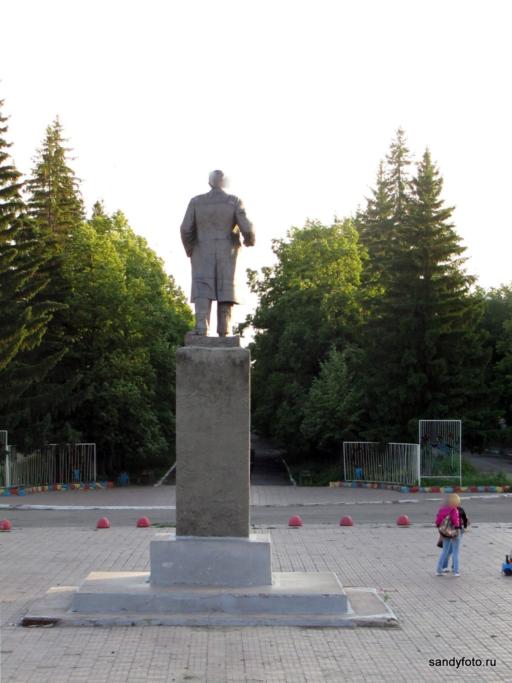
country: RU
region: Chelyabinsk
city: Troitsk
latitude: 54.0465
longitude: 61.6297
